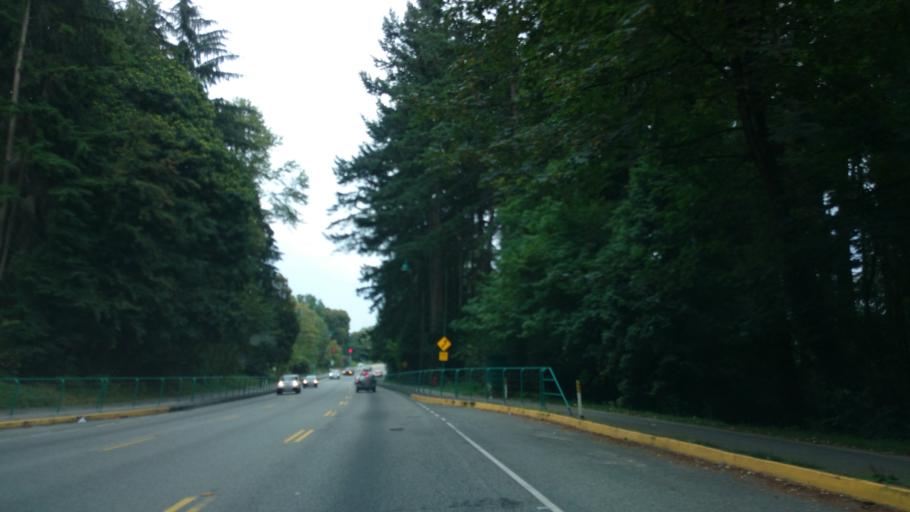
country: CA
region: British Columbia
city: West End
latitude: 49.2987
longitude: -123.1398
